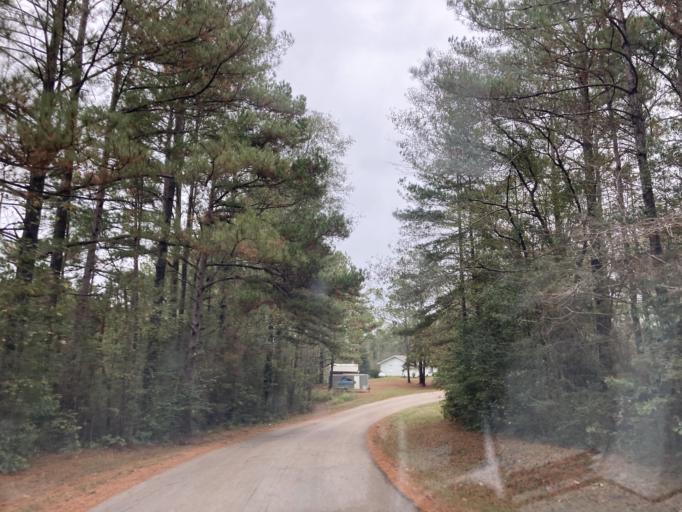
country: US
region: Mississippi
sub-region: Lamar County
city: Purvis
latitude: 31.2470
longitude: -89.5044
